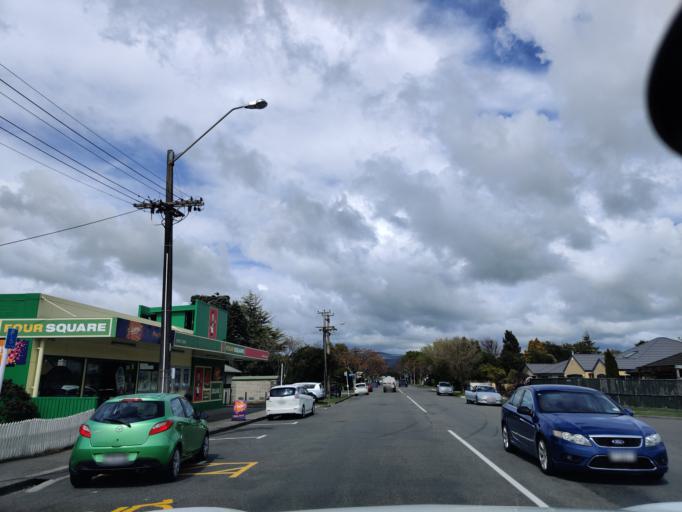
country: NZ
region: Manawatu-Wanganui
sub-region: Palmerston North City
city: Palmerston North
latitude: -40.3795
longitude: 175.5848
